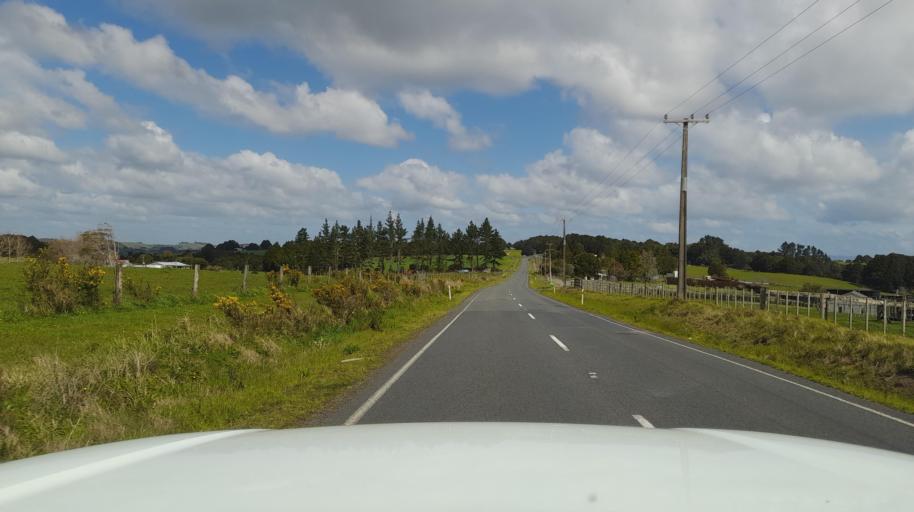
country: NZ
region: Northland
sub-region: Far North District
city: Waimate North
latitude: -35.2846
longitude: 173.8284
